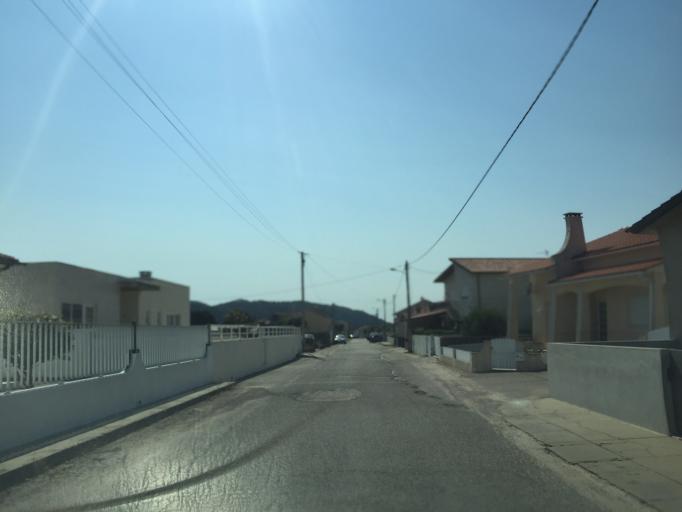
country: PT
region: Coimbra
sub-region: Figueira da Foz
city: Tavarede
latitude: 40.2167
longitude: -8.8438
